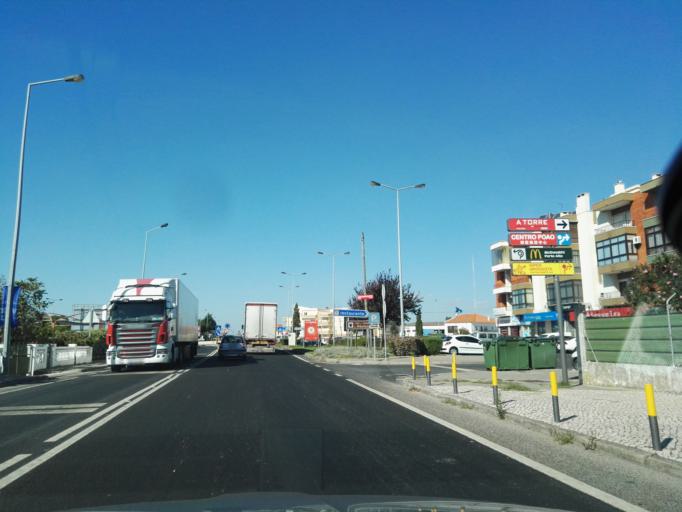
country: PT
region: Santarem
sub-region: Benavente
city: Samora Correia
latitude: 38.9204
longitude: -8.8816
